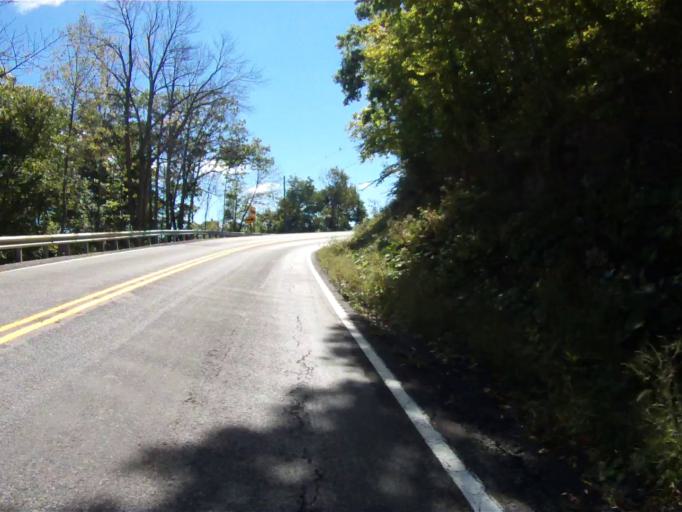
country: US
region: Pennsylvania
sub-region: Centre County
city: Park Forest Village
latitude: 40.9239
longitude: -77.9467
